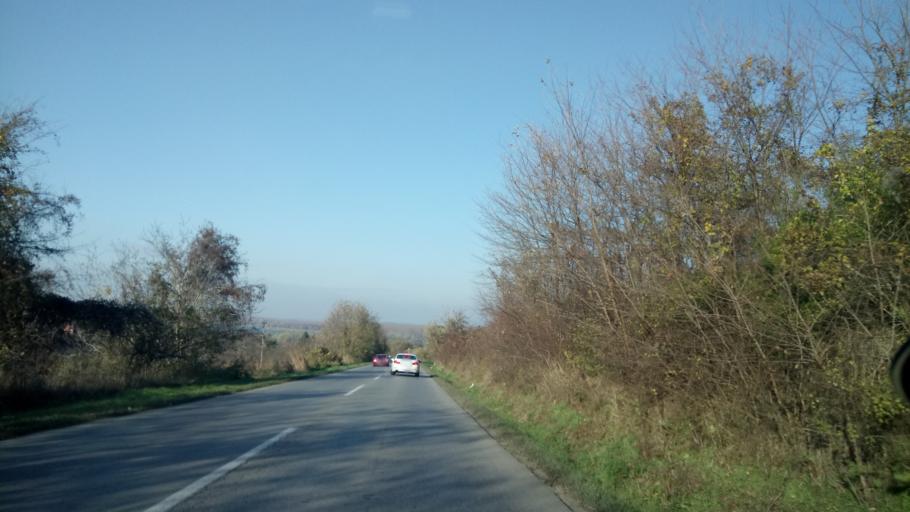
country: RS
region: Autonomna Pokrajina Vojvodina
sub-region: Juznobacki Okrug
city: Sremski Karlovci
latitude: 45.1844
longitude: 19.9535
